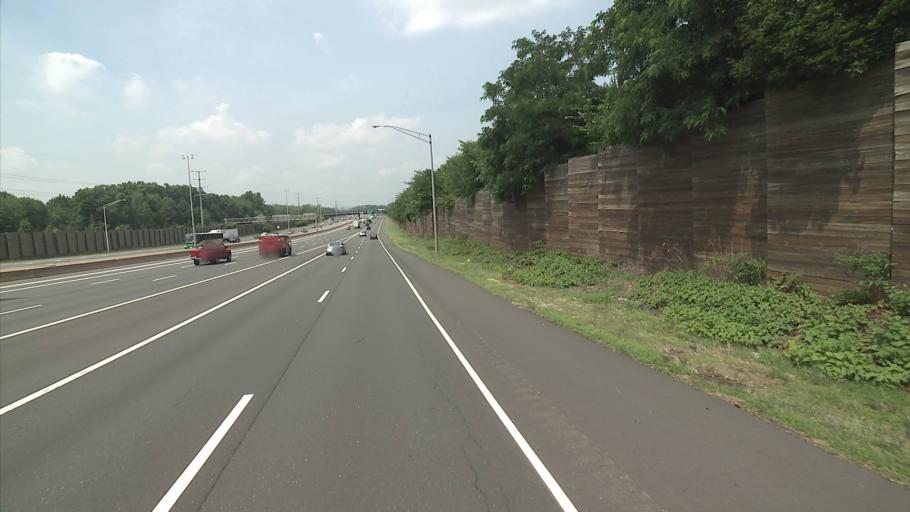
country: US
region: Connecticut
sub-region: Hartford County
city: East Hartford
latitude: 41.7726
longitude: -72.5954
